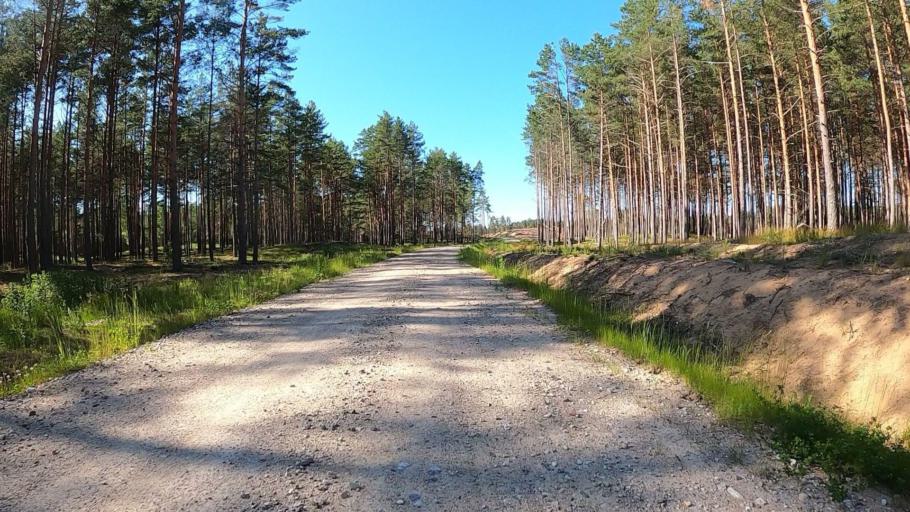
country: LV
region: Carnikava
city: Carnikava
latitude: 57.0909
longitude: 24.2473
